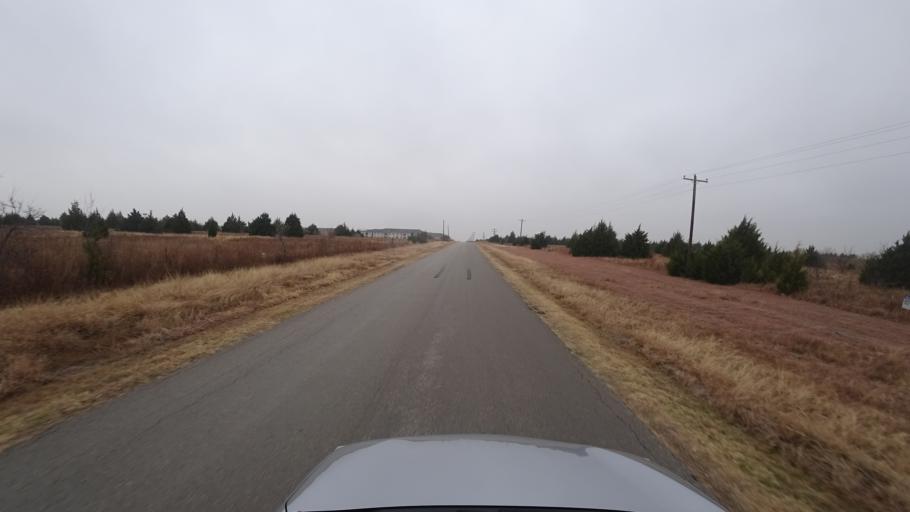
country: US
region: Texas
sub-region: Denton County
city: The Colony
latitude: 33.0680
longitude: -96.9172
